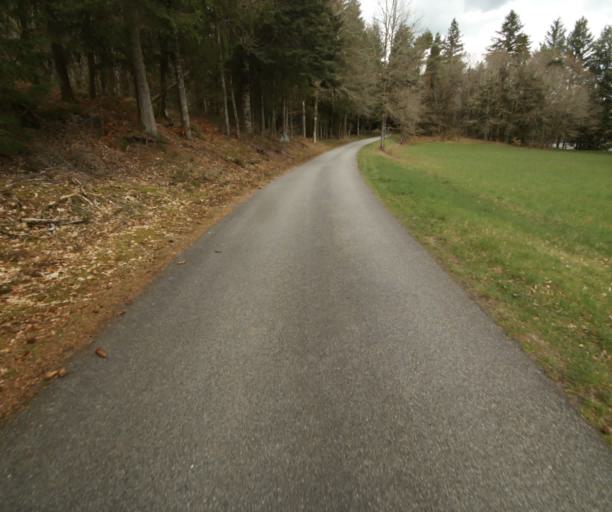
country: FR
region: Limousin
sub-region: Departement de la Correze
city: Correze
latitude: 45.3350
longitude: 1.9512
